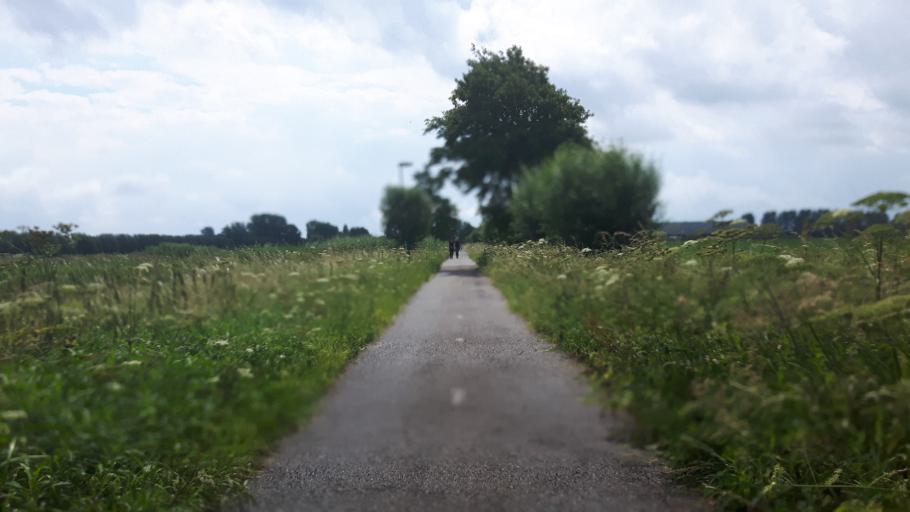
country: NL
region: Utrecht
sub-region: Gemeente Oudewater
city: Oudewater
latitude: 52.0100
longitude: 4.8853
